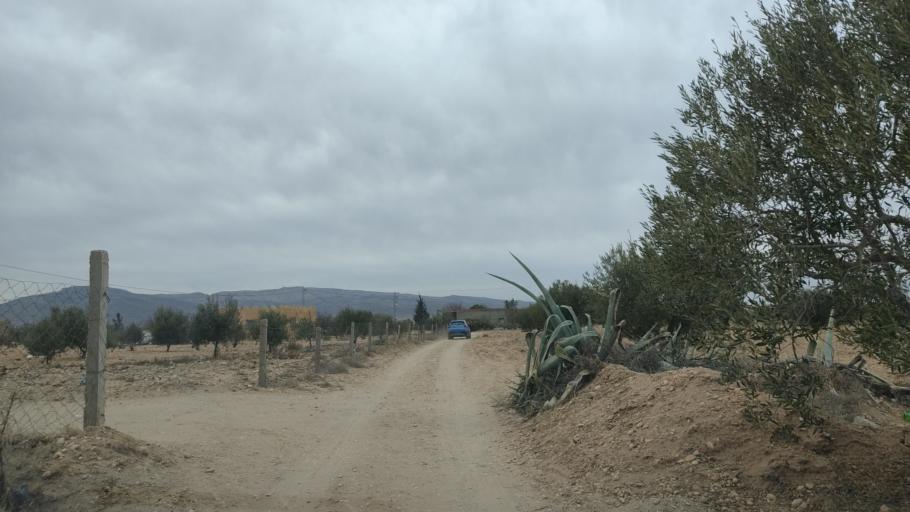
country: TN
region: Al Qasrayn
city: Kasserine
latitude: 35.2292
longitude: 8.9263
